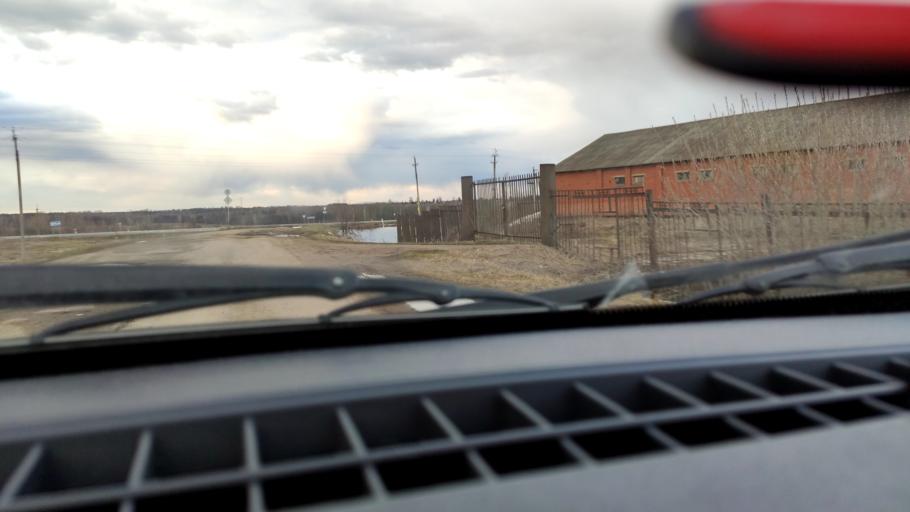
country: RU
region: Bashkortostan
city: Kudeyevskiy
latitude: 54.8156
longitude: 56.7558
